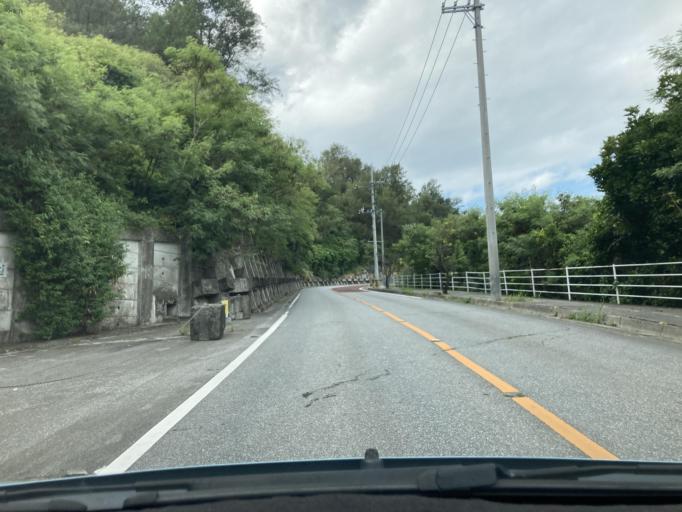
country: JP
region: Okinawa
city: Ginowan
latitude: 26.2608
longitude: 127.7844
